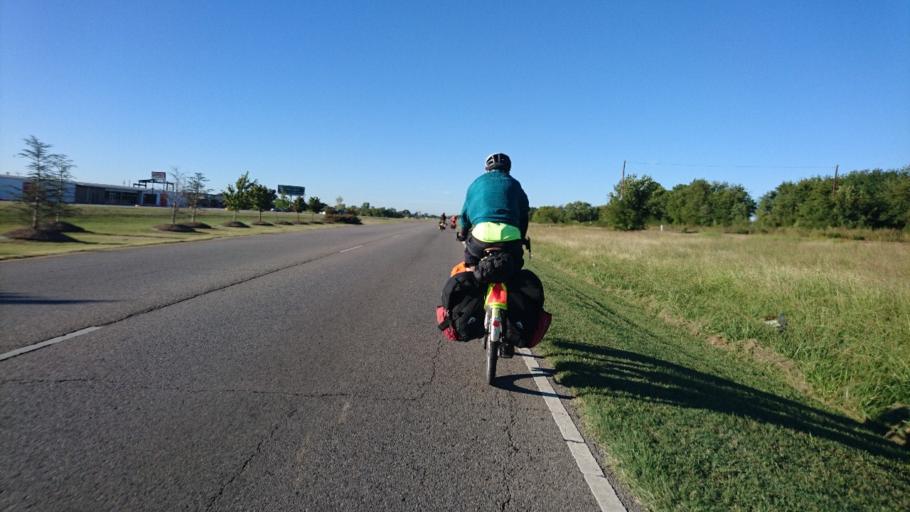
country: US
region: Oklahoma
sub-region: Rogers County
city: Claremore
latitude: 36.2861
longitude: -95.6357
